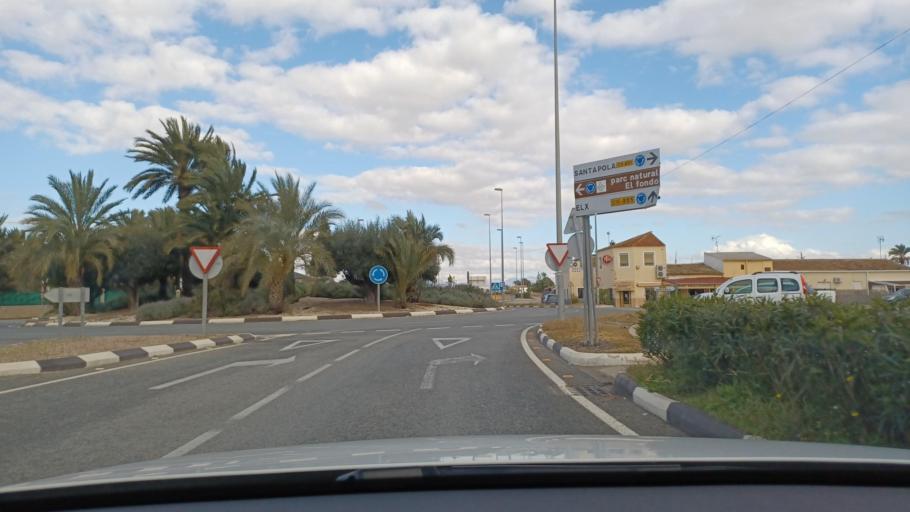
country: ES
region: Valencia
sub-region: Provincia de Alicante
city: Elche
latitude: 38.1870
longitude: -0.7014
